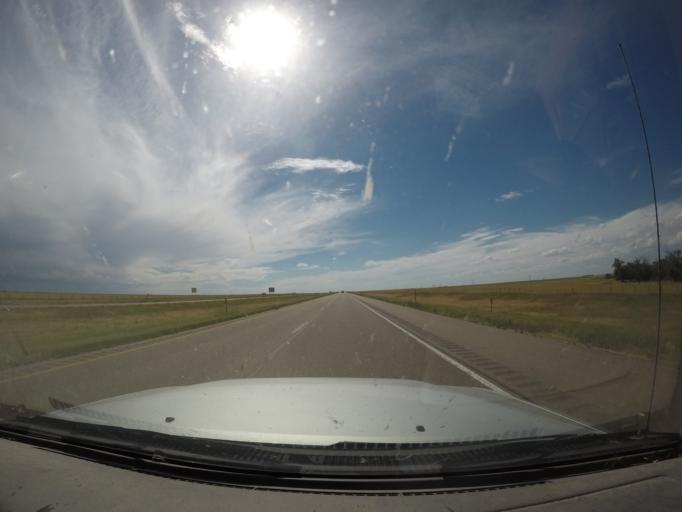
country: US
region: Colorado
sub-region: Sedgwick County
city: Julesburg
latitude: 41.0488
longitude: -102.3485
